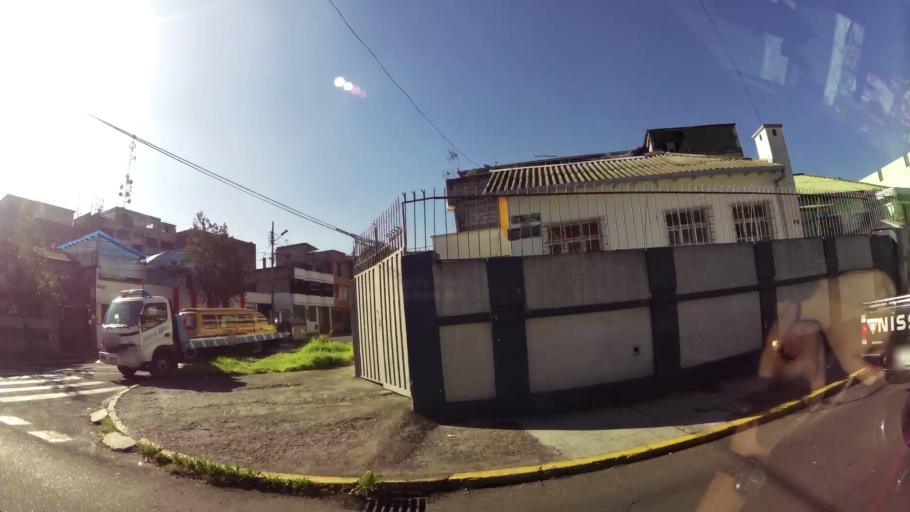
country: EC
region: Pichincha
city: Quito
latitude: -0.2429
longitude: -78.5219
